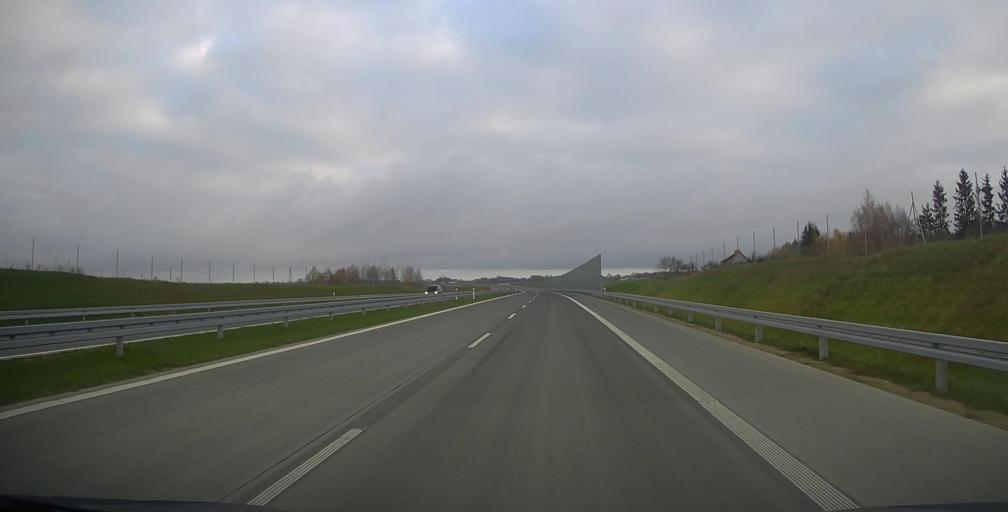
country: PL
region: Podlasie
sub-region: Powiat suwalski
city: Raczki
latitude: 53.9252
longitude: 22.7509
